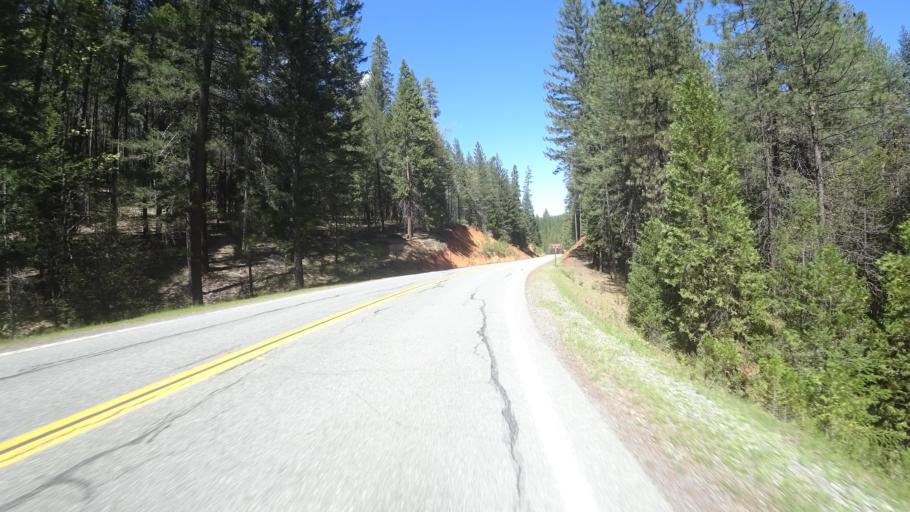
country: US
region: California
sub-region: Trinity County
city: Lewiston
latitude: 40.8585
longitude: -122.8200
